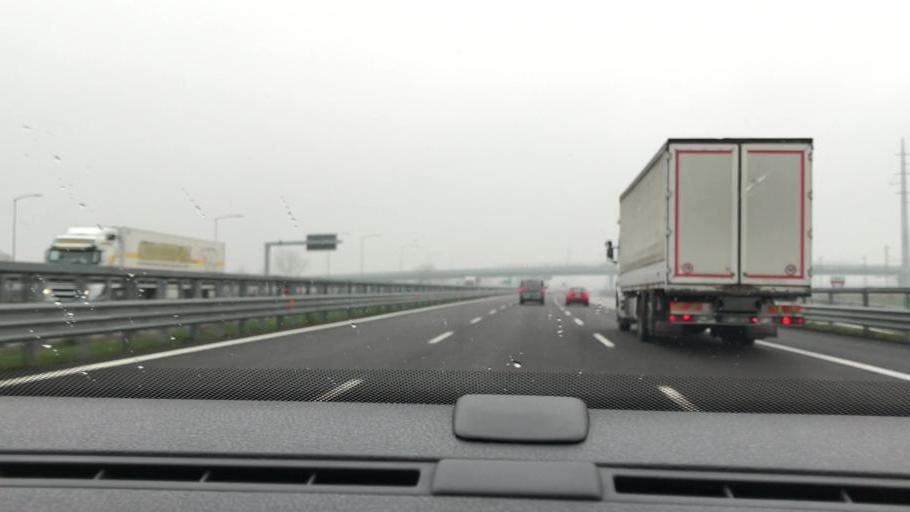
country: IT
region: Lombardy
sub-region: Provincia di Bergamo
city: Bariano
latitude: 45.5077
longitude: 9.6927
